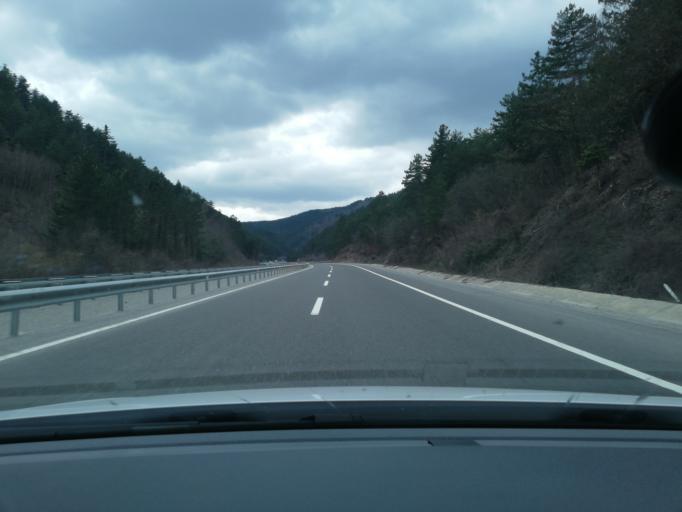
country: TR
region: Bolu
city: Yenicaga
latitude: 40.8484
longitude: 32.0652
